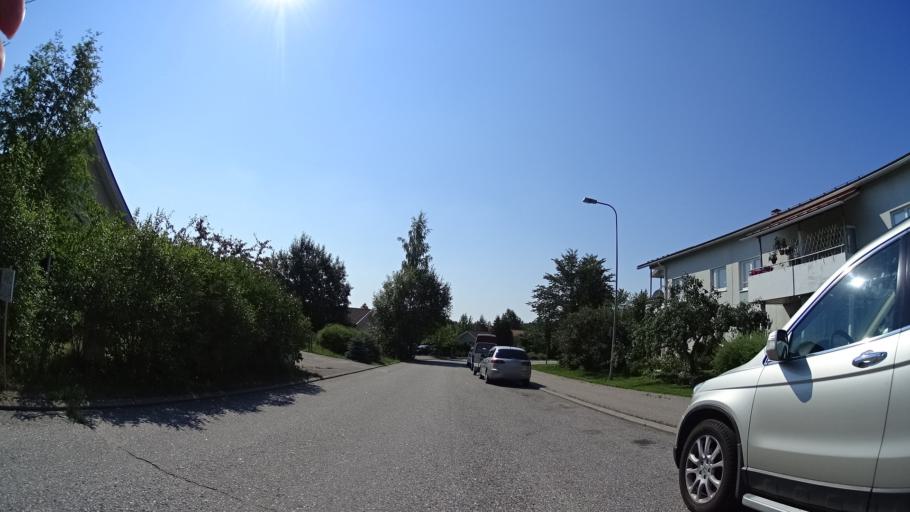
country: FI
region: Uusimaa
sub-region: Helsinki
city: Kerava
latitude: 60.3666
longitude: 25.0781
